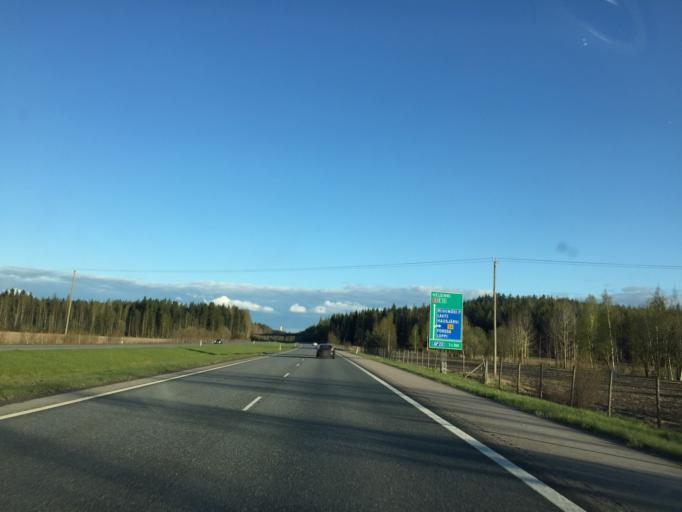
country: FI
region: Haeme
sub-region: Riihimaeki
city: Riihimaeki
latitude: 60.7700
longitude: 24.7167
